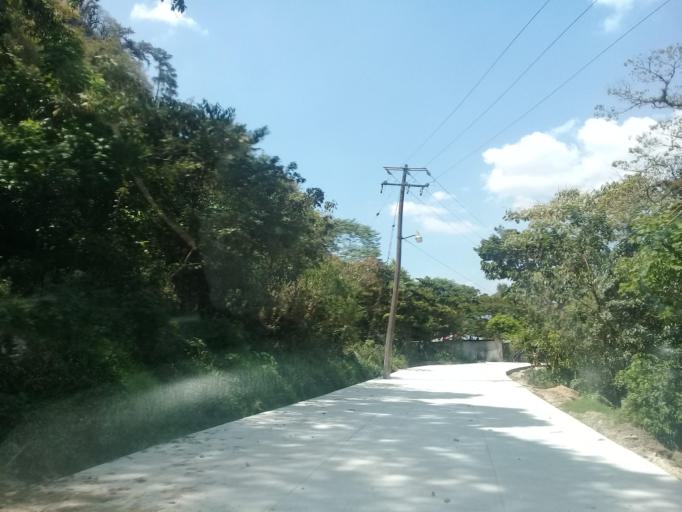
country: MX
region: Veracruz
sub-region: Tlilapan
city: Tonalixco
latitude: 18.8069
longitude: -97.0643
